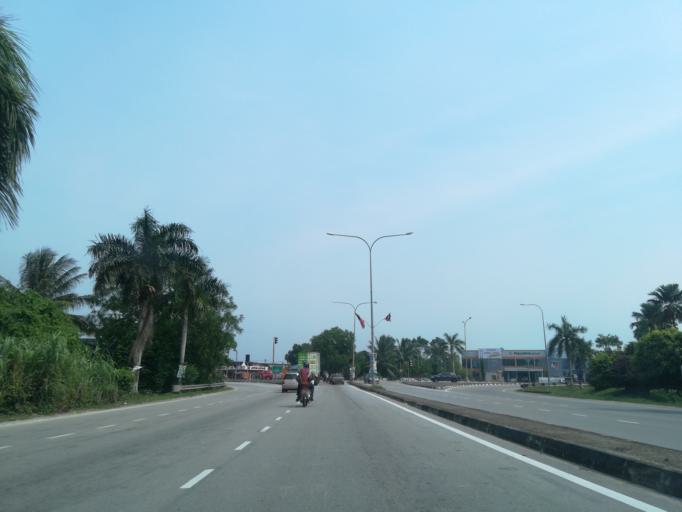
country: MY
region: Kedah
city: Kulim
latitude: 5.4322
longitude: 100.5515
